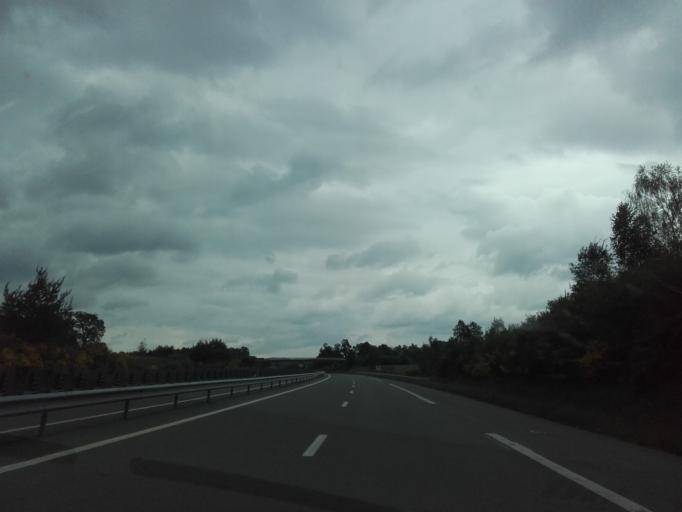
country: FR
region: Limousin
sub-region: Departement de la Correze
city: Correze
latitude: 45.3233
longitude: 1.8886
